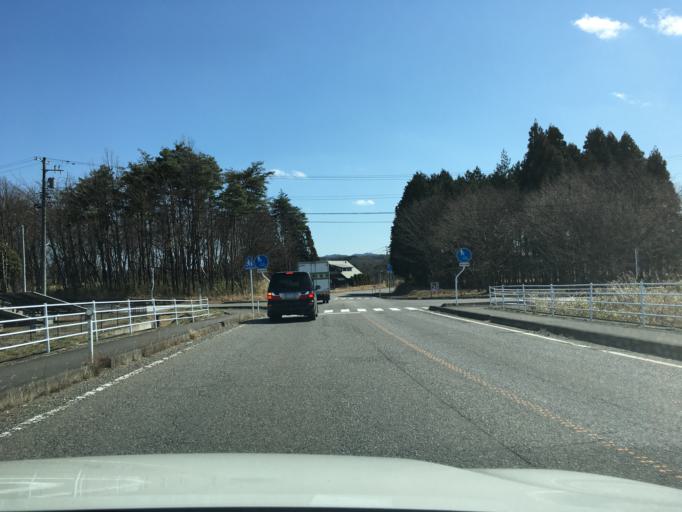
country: JP
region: Tochigi
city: Kuroiso
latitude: 37.0996
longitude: 140.1882
